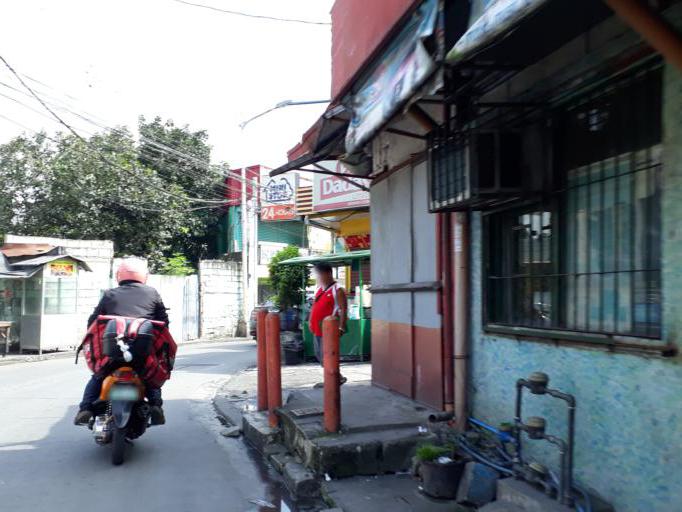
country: PH
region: Calabarzon
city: Bagong Pagasa
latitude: 14.6757
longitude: 121.0043
